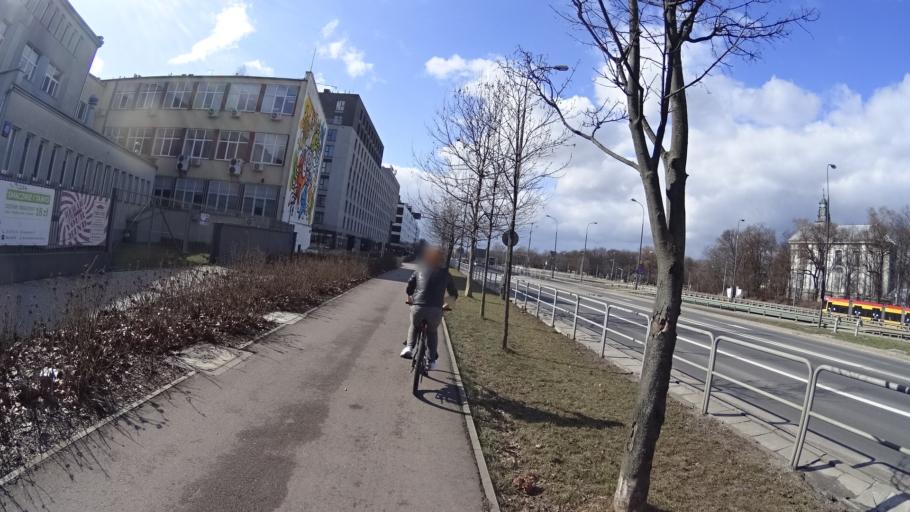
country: PL
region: Masovian Voivodeship
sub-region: Warszawa
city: Ochota
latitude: 52.2261
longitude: 20.9458
